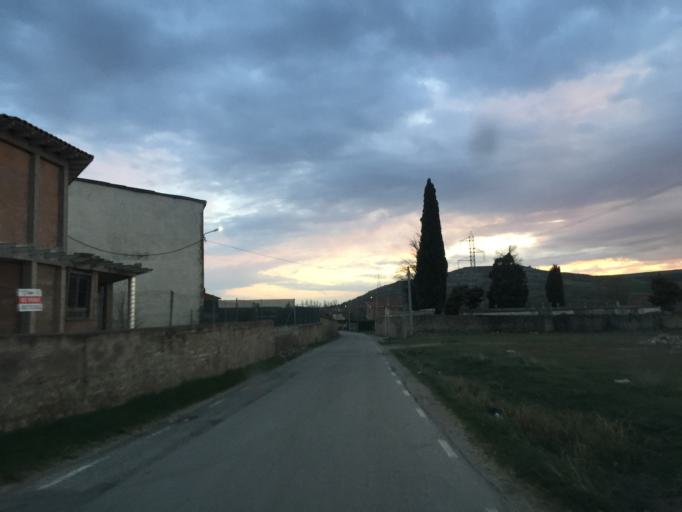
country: ES
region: Castille and Leon
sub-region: Provincia de Burgos
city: Tardajos
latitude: 42.3508
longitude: -3.8198
